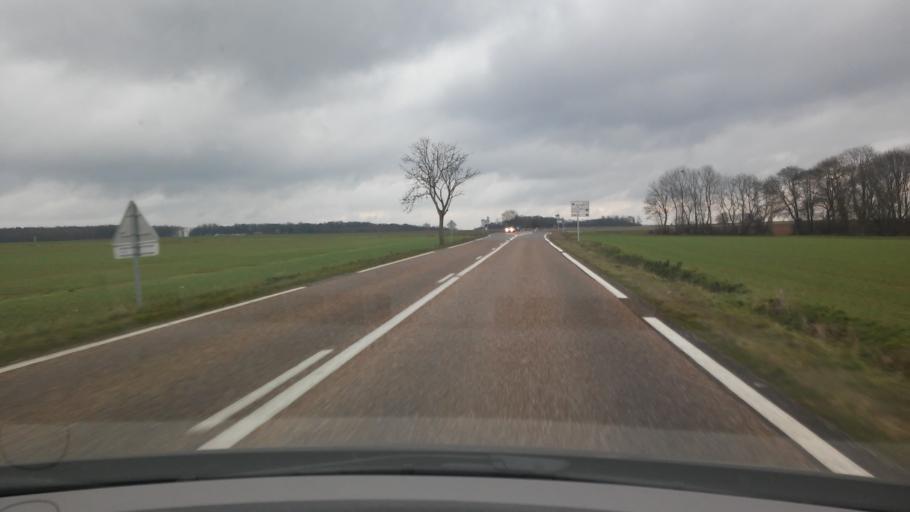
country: FR
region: Lorraine
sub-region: Departement de la Moselle
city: Retonfey
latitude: 49.1171
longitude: 6.3162
